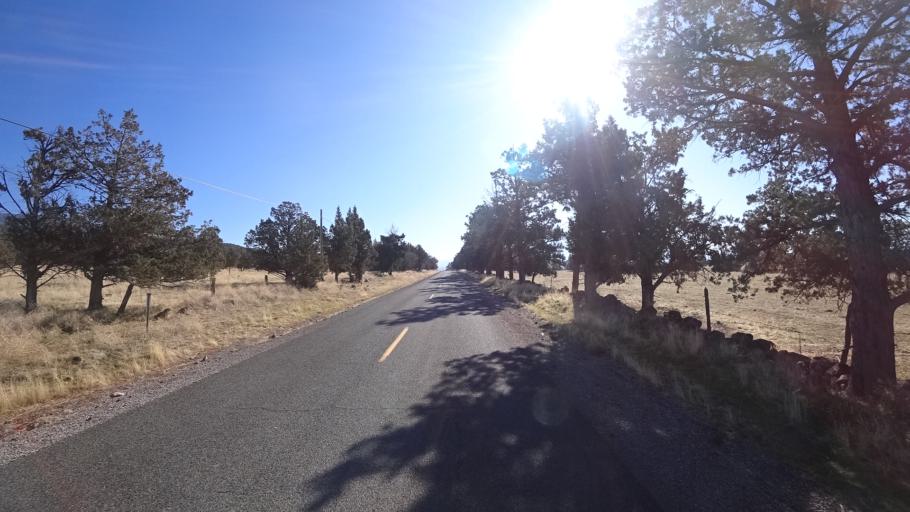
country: US
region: California
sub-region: Siskiyou County
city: Weed
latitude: 41.6250
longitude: -122.3283
